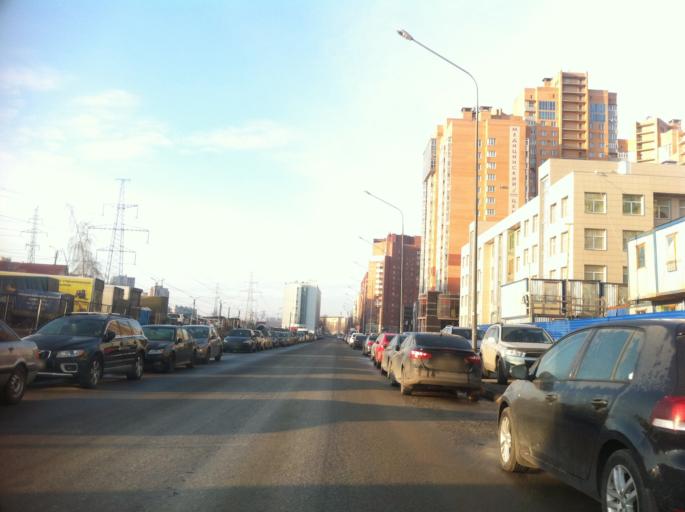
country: RU
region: St.-Petersburg
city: Uritsk
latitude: 59.8591
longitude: 30.2019
